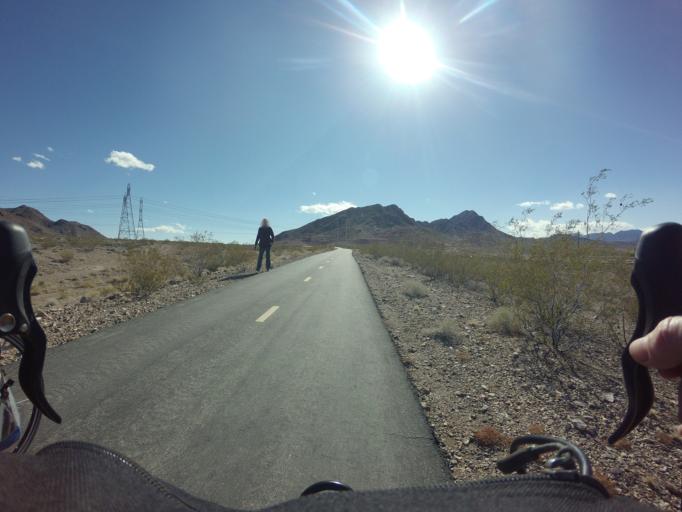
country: US
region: Nevada
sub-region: Clark County
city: Henderson
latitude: 35.9877
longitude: -114.9205
